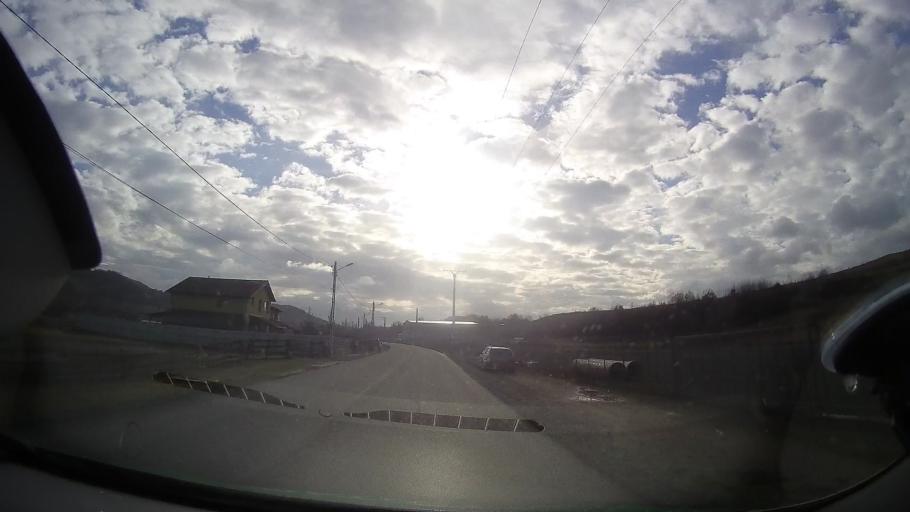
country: RO
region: Cluj
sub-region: Comuna Floresti
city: Luna de Sus
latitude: 46.7208
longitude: 23.4235
